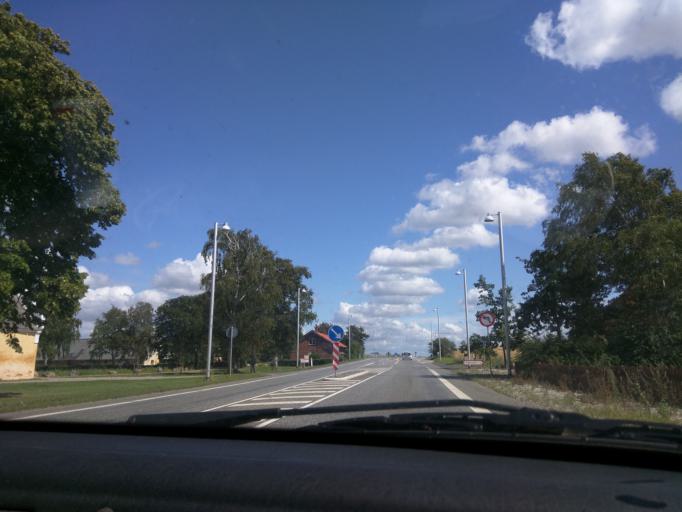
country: DK
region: Zealand
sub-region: Kalundborg Kommune
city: Svebolle
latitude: 55.6722
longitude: 11.2057
